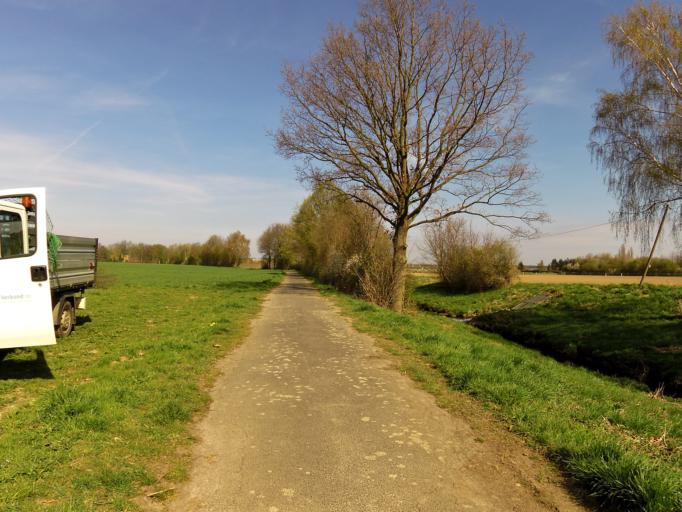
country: DE
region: North Rhine-Westphalia
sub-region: Regierungsbezirk Koln
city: Rheinbach
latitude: 50.6522
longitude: 6.9823
